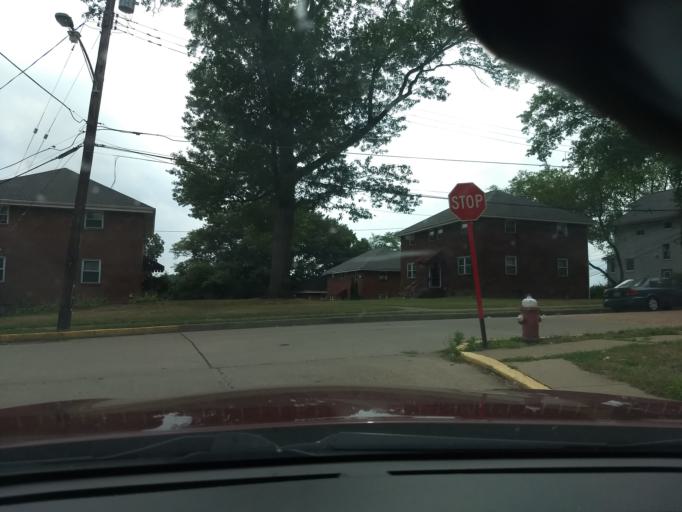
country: US
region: Pennsylvania
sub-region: Allegheny County
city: Avalon
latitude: 40.4948
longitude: -80.0625
